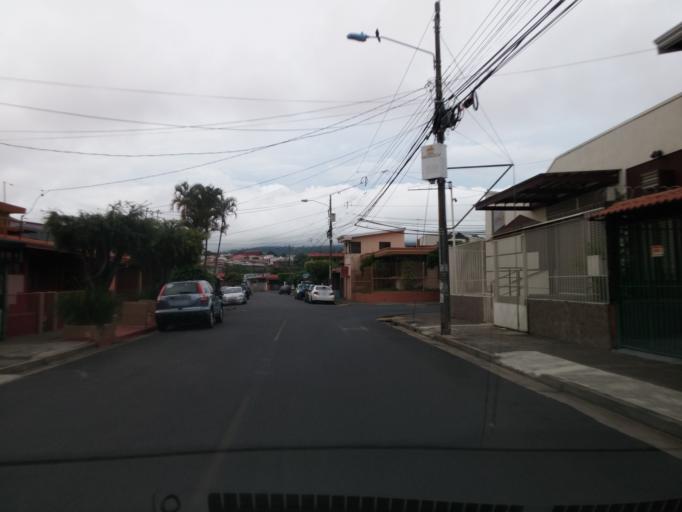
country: CR
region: Heredia
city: San Francisco
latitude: 10.0001
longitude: -84.1248
